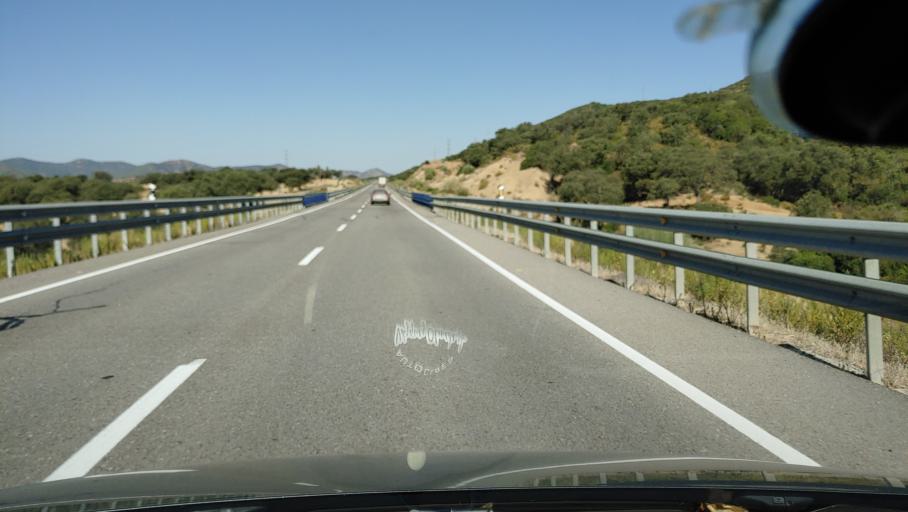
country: ES
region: Andalusia
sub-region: Province of Cordoba
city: Villaharta
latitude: 38.1336
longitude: -4.9425
